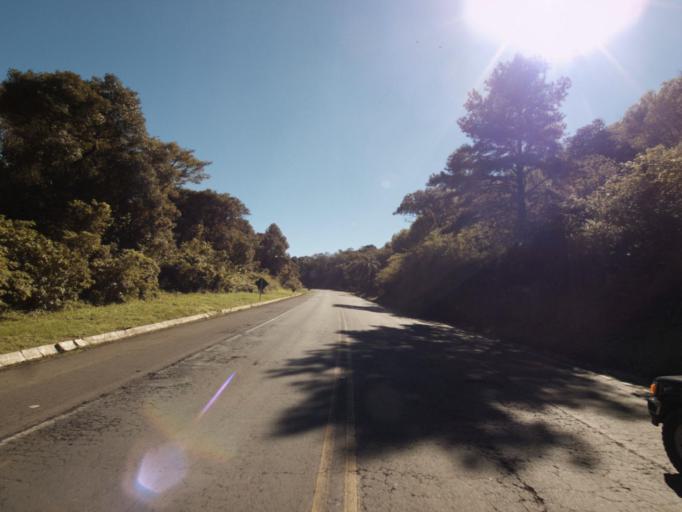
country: BR
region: Rio Grande do Sul
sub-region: Frederico Westphalen
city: Frederico Westphalen
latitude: -26.8405
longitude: -53.1720
